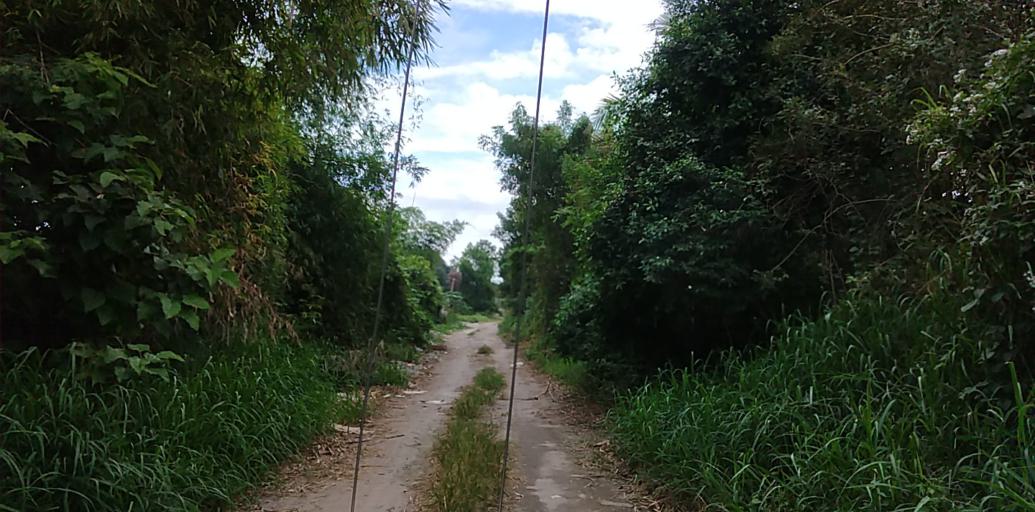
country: PH
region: Central Luzon
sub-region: Province of Pampanga
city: Pulung Santol
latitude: 15.0358
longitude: 120.5612
